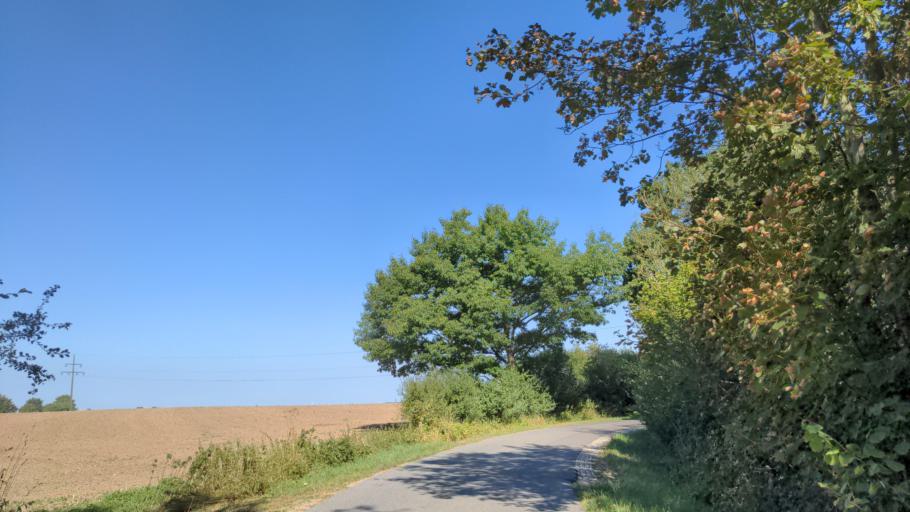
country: DE
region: Schleswig-Holstein
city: Gross Disnack
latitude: 53.7554
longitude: 10.6819
